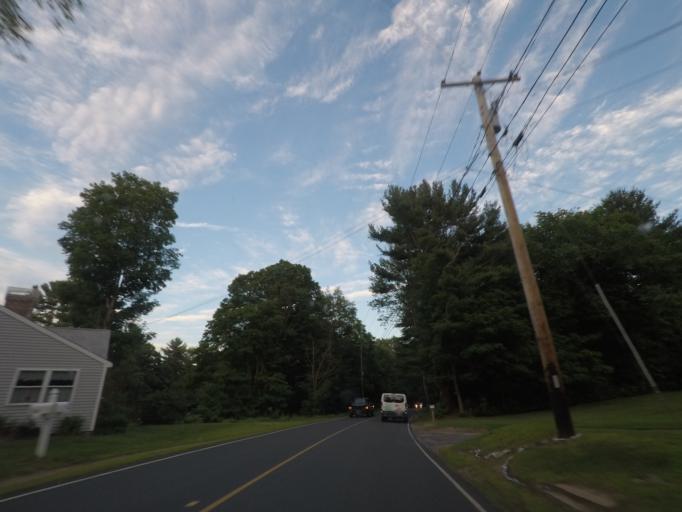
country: US
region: Massachusetts
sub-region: Worcester County
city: Fiskdale
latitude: 42.1538
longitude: -72.1408
